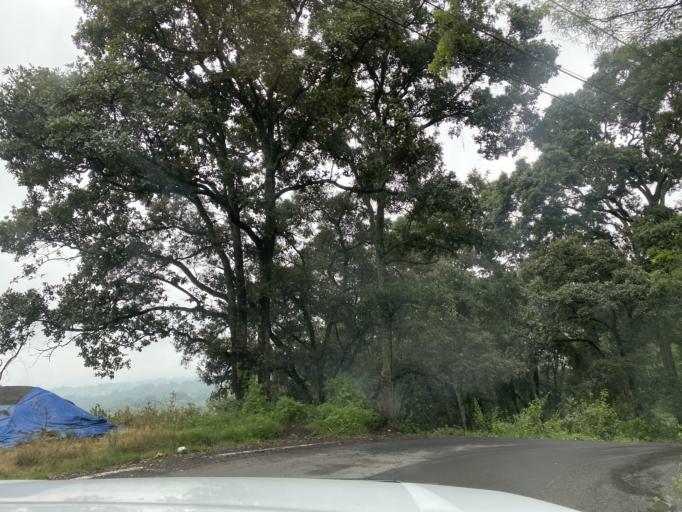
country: MX
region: Mexico
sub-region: Ozumba
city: San Jose Tlacotitlan
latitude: 18.9874
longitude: -98.8183
